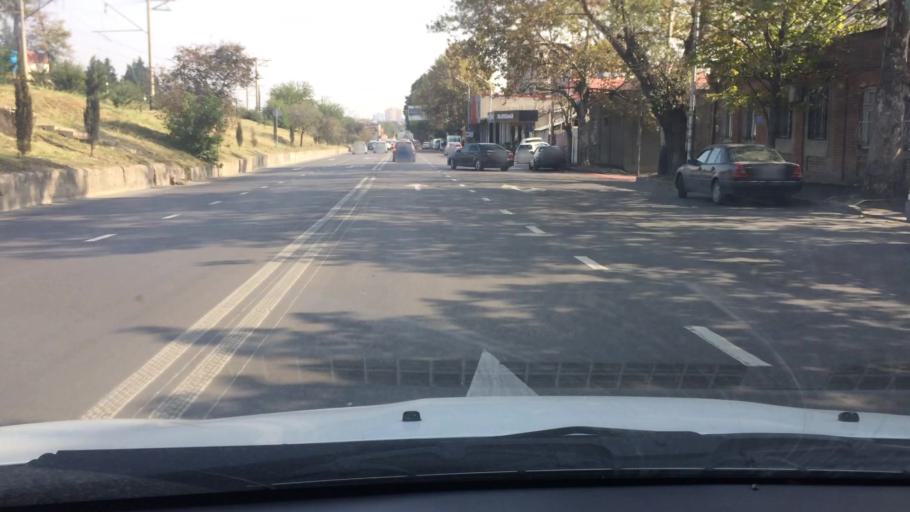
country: GE
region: T'bilisi
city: Tbilisi
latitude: 41.6916
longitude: 44.8306
